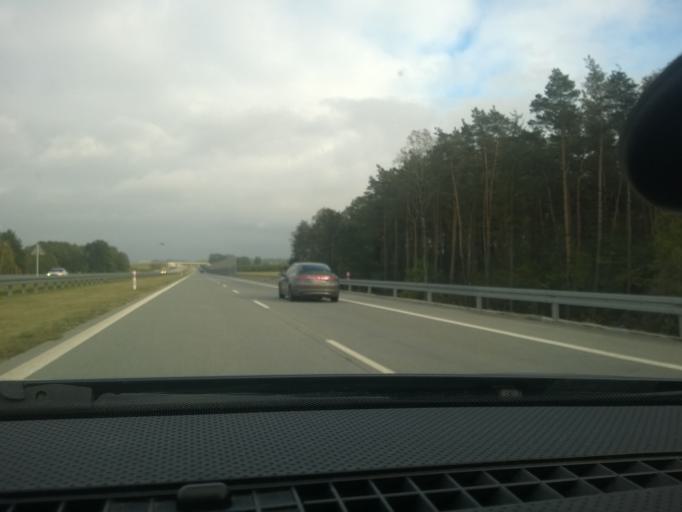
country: PL
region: Lodz Voivodeship
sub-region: Powiat pabianicki
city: Pabianice
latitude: 51.6080
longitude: 19.3265
